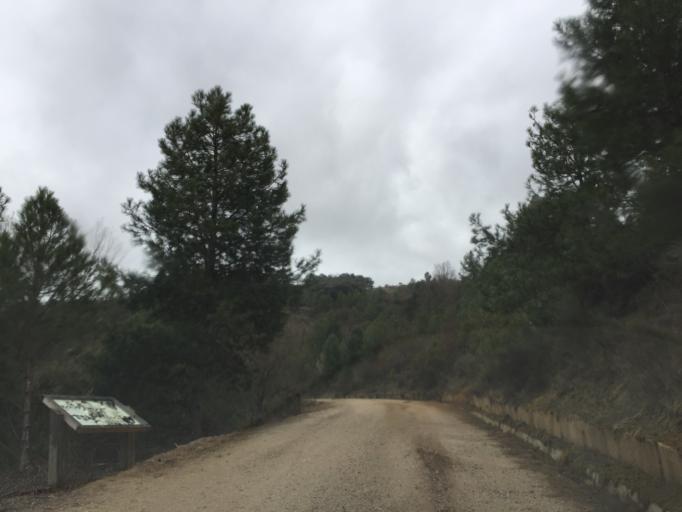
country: ES
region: Castille and Leon
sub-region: Provincia de Leon
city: Leon
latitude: 42.5978
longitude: -5.5398
